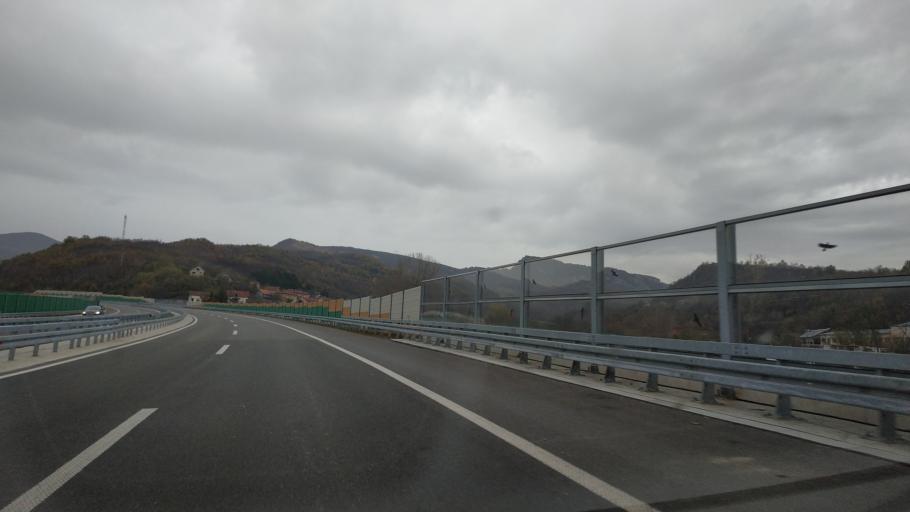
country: RS
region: Central Serbia
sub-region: Nisavski Okrug
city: Niska Banja
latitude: 43.3006
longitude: 22.0471
